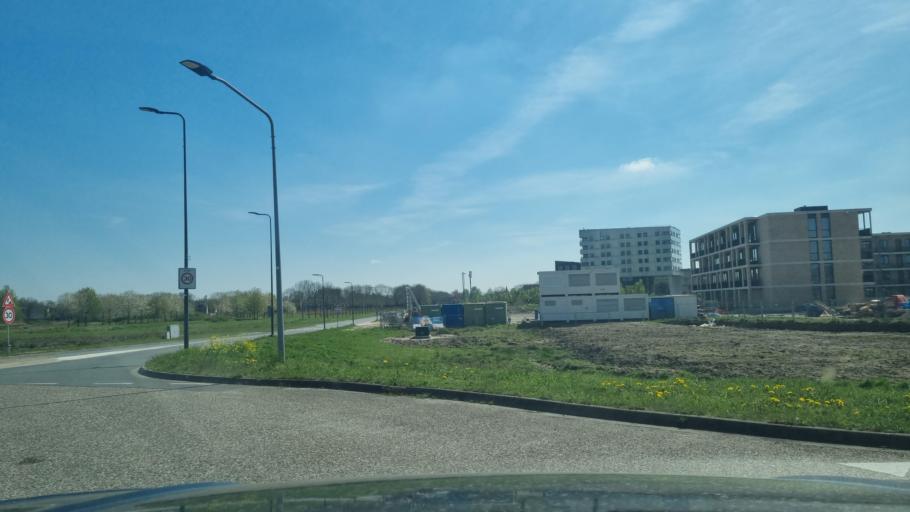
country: NL
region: North Brabant
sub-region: Gemeente 's-Hertogenbosch
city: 's-Hertogenbosch
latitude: 51.7288
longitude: 5.3574
